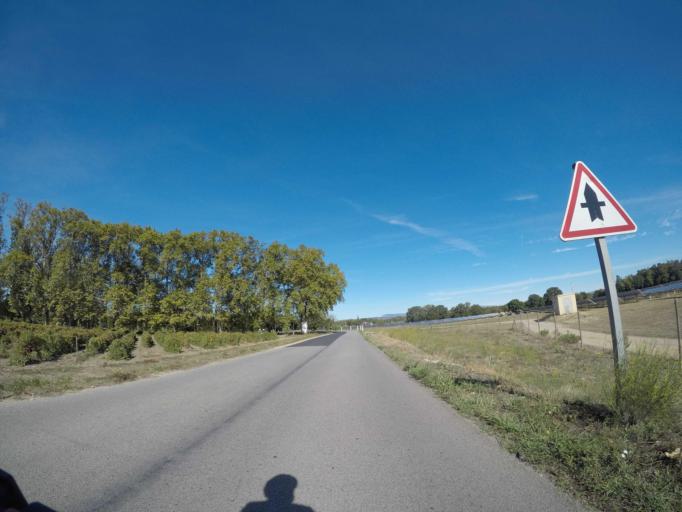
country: FR
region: Languedoc-Roussillon
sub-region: Departement des Pyrenees-Orientales
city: Le Soler
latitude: 42.6645
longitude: 2.7939
